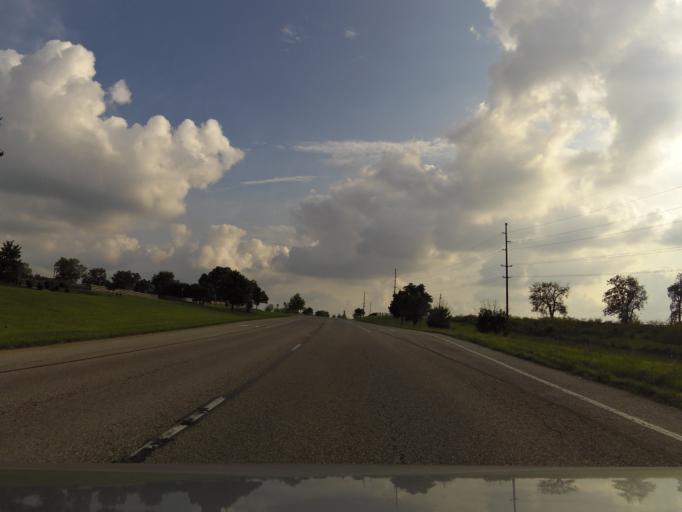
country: US
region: Kentucky
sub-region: Bourbon County
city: Paris
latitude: 38.1549
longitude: -84.3368
